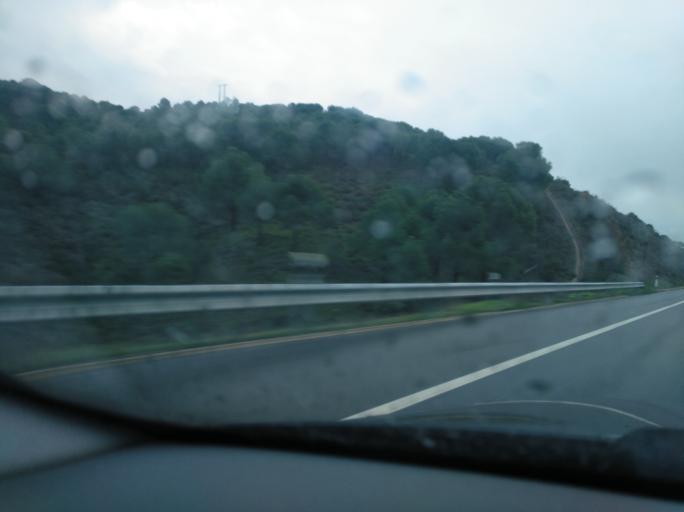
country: PT
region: Faro
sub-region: Alcoutim
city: Alcoutim
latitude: 37.3452
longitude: -7.5069
